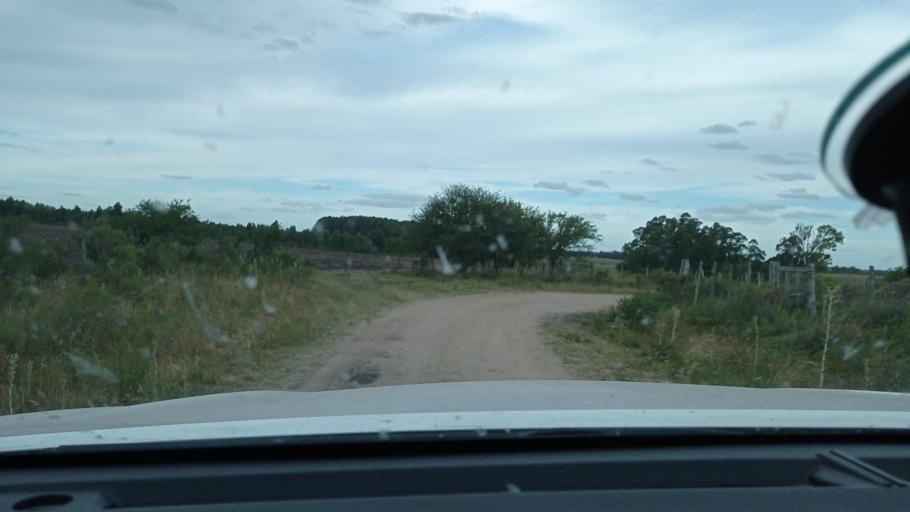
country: UY
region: Florida
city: Casupa
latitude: -34.1190
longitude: -55.8161
